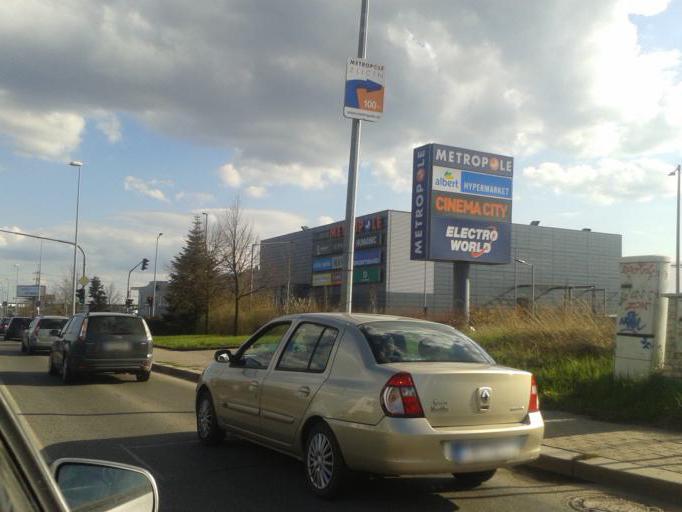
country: CZ
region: Central Bohemia
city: Hostivice
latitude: 50.0556
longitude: 14.2883
